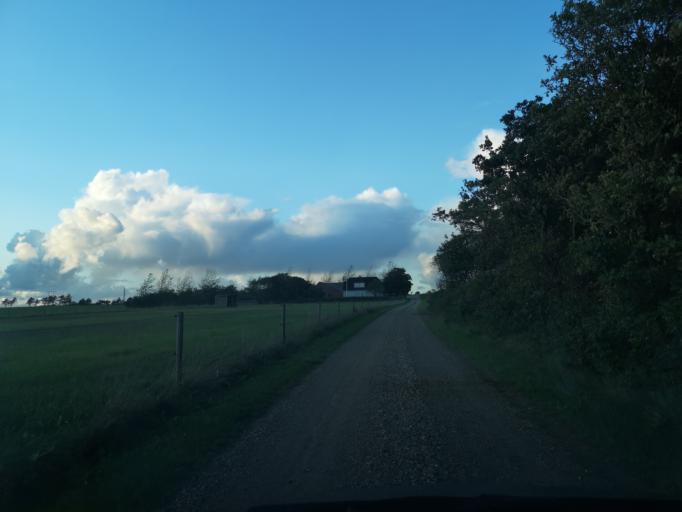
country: DK
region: Central Jutland
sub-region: Ringkobing-Skjern Kommune
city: Videbaek
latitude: 56.0473
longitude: 8.5884
